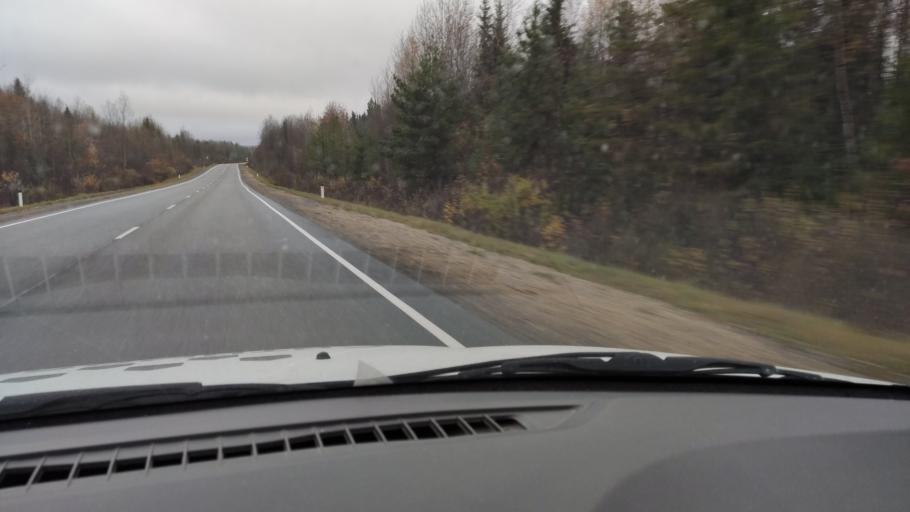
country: RU
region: Kirov
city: Omutninsk
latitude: 58.7047
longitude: 52.1067
